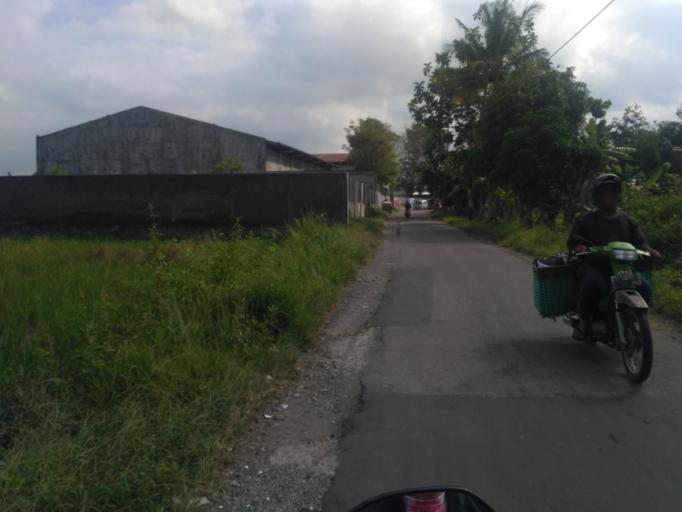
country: ID
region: Daerah Istimewa Yogyakarta
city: Yogyakarta
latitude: -7.7637
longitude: 110.3586
